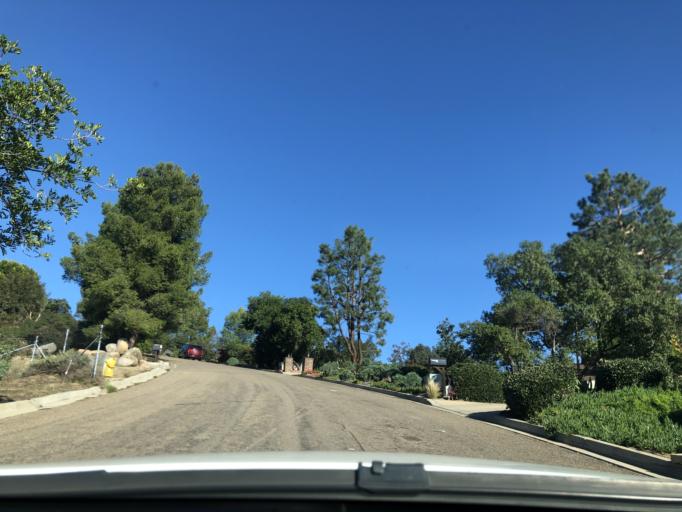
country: US
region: California
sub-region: San Diego County
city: Bostonia
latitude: 32.7802
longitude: -116.9390
